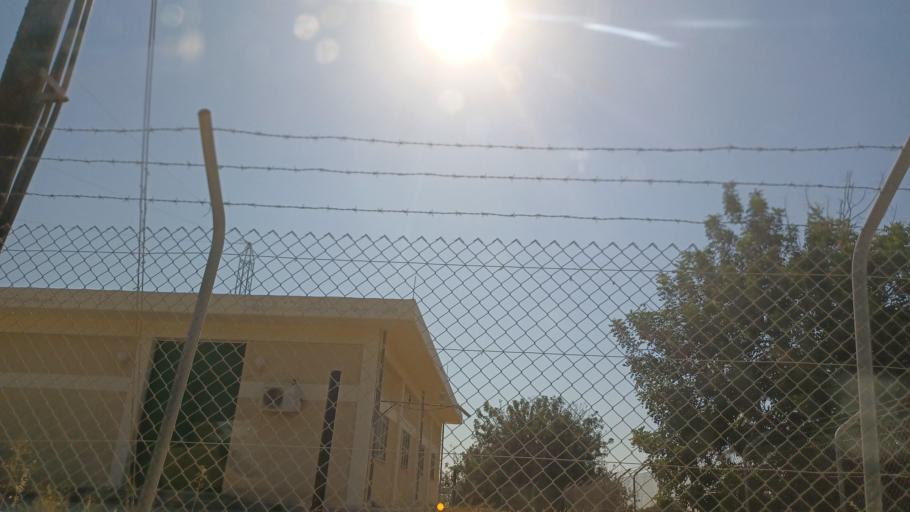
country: CY
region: Limassol
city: Pissouri
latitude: 34.6819
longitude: 32.7397
